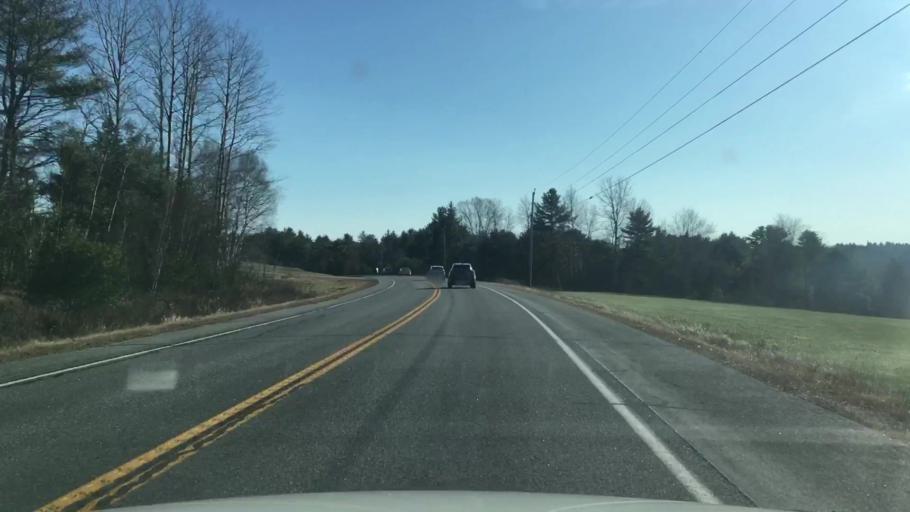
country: US
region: Maine
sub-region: Knox County
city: Washington
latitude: 44.2322
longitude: -69.3518
